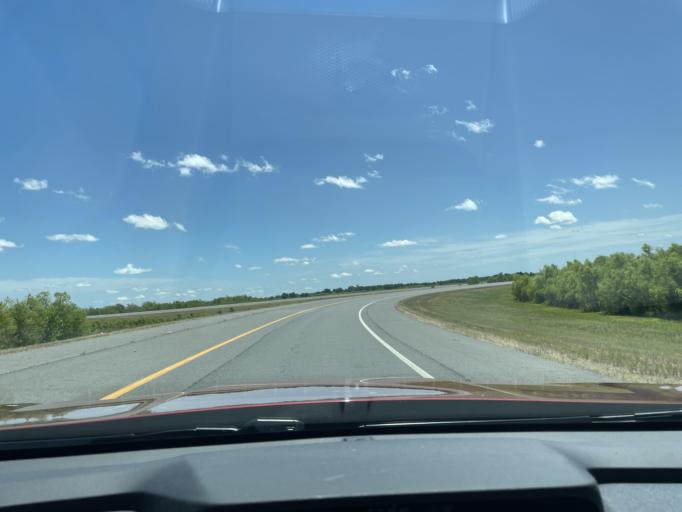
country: US
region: Arkansas
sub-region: Jefferson County
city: Pine Bluff
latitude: 34.1736
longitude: -91.9890
